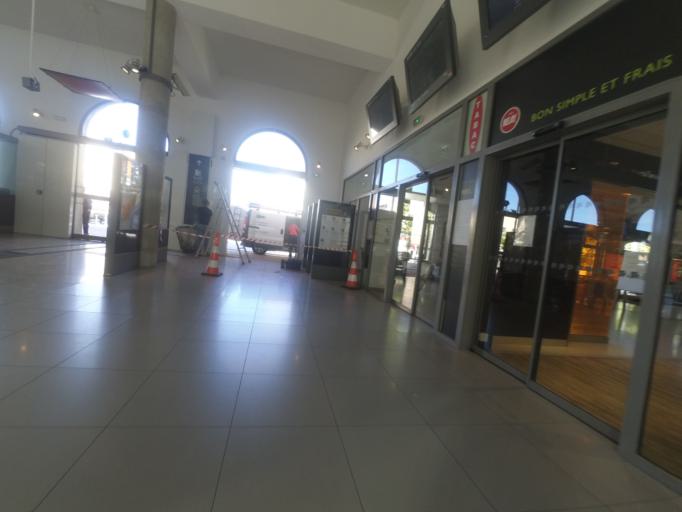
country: FR
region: Languedoc-Roussillon
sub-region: Departement des Pyrenees-Orientales
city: Perpignan
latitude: 42.6962
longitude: 2.8797
